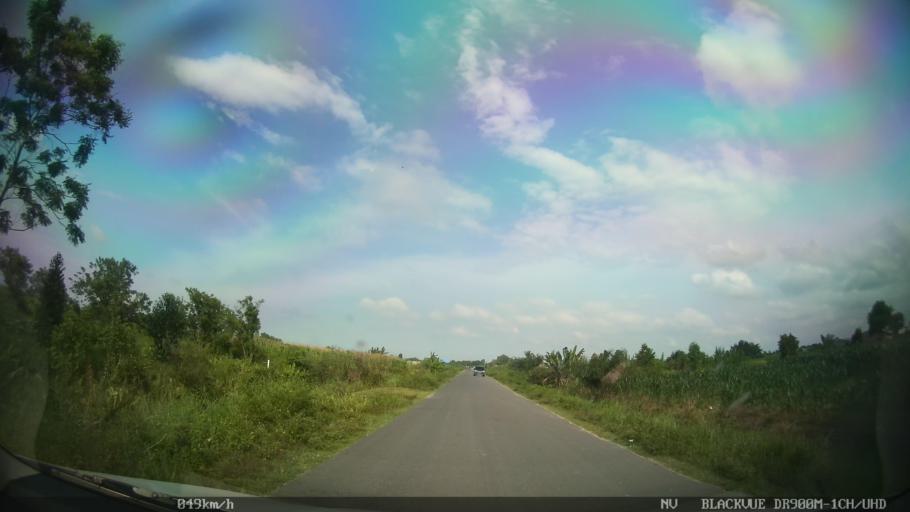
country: ID
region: North Sumatra
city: Medan
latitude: 3.5729
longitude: 98.7666
